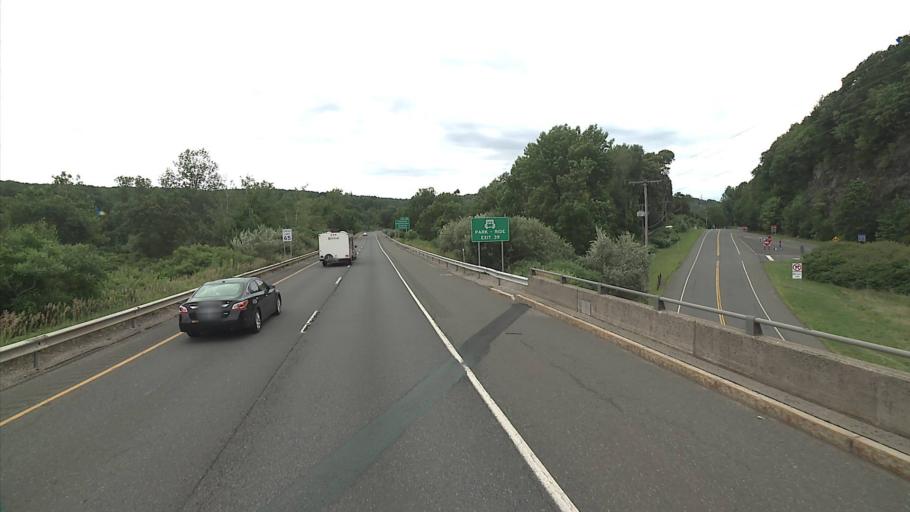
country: US
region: Connecticut
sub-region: Litchfield County
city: Thomaston
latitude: 41.6827
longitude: -73.0670
